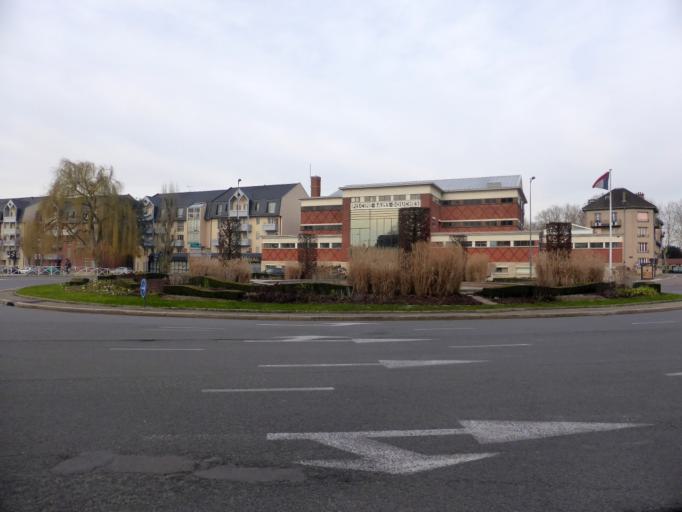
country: FR
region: Champagne-Ardenne
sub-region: Departement de l'Aube
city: Troyes
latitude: 48.2950
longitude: 4.0810
